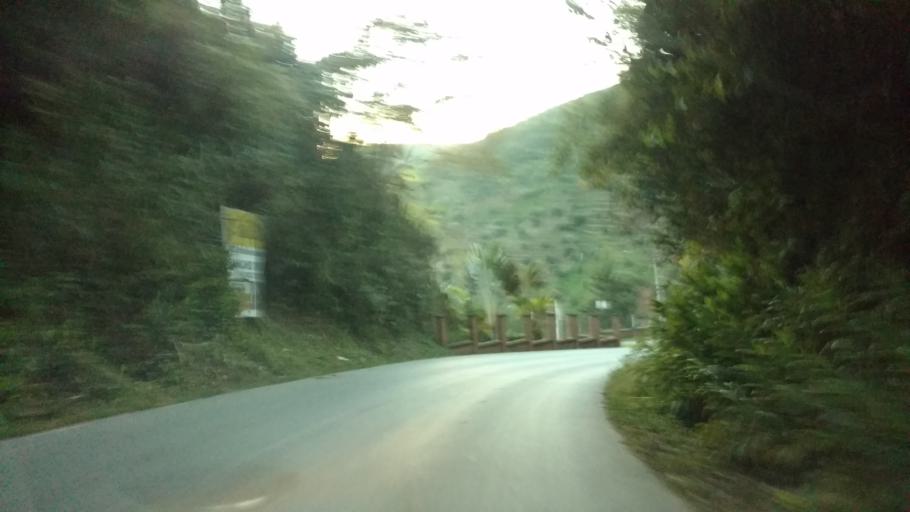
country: CO
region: Caldas
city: Aranzazu
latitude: 5.2659
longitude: -75.4951
